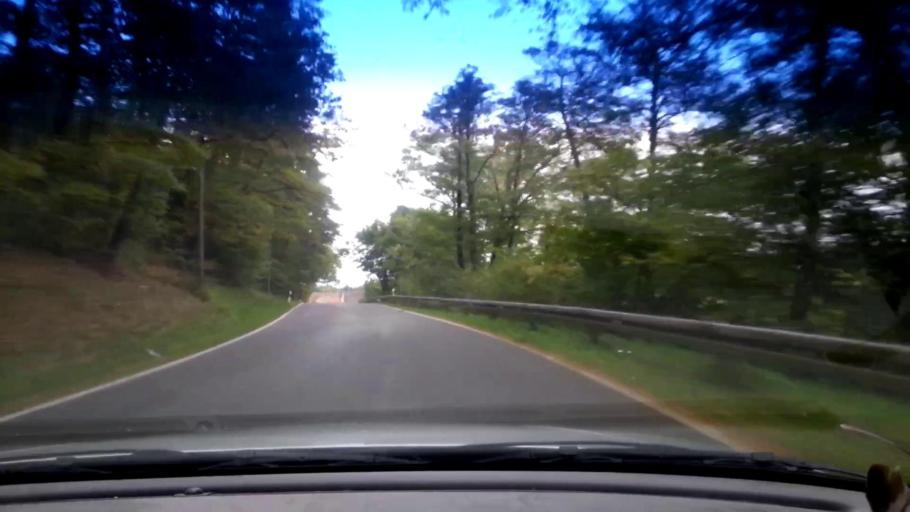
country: DE
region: Bavaria
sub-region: Upper Franconia
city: Lauter
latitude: 49.9840
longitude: 10.7661
